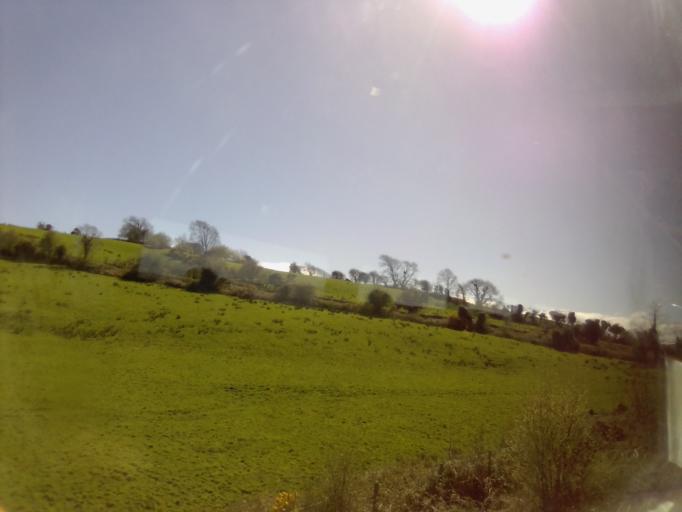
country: IE
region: Munster
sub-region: Ciarrai
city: Castleisland
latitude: 52.1679
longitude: -9.5730
